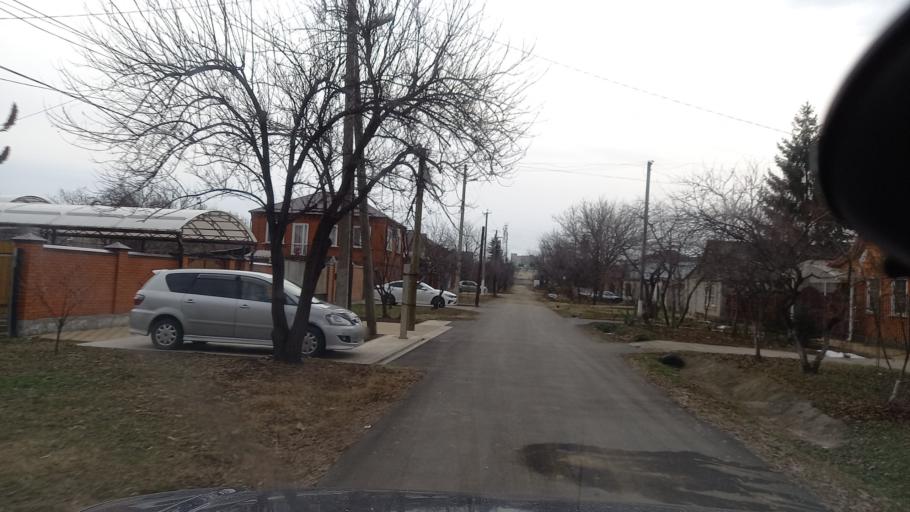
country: RU
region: Adygeya
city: Maykop
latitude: 44.5919
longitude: 40.0985
